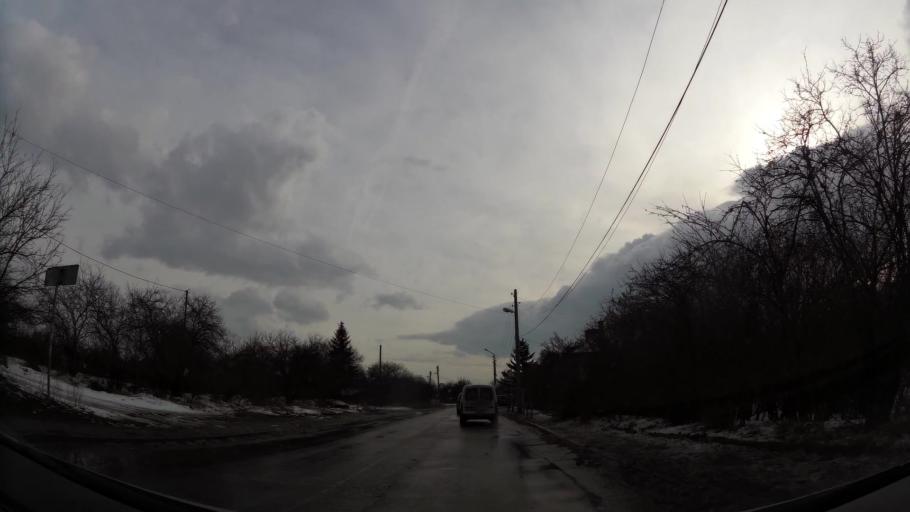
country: BG
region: Sofia-Capital
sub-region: Stolichna Obshtina
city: Sofia
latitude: 42.7020
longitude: 23.3872
